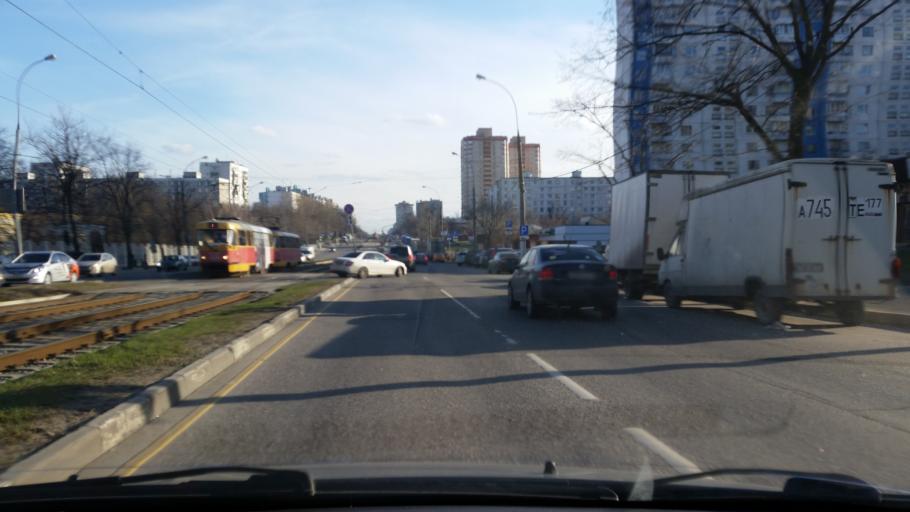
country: RU
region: Moscow
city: Chertanovo Yuzhnoye
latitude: 55.6191
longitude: 37.5935
